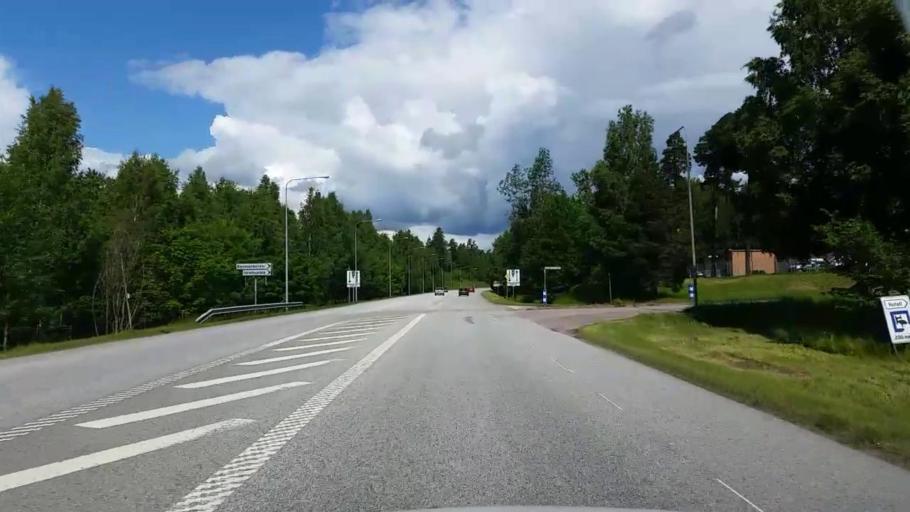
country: SE
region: Vaestmanland
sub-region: Fagersta Kommun
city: Fagersta
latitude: 60.0075
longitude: 15.7850
